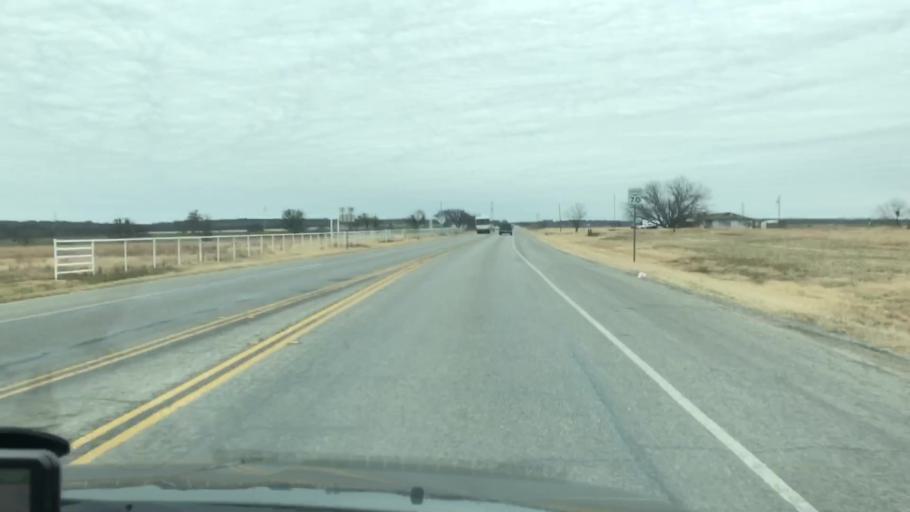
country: US
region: Texas
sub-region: Palo Pinto County
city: Mineral Wells
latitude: 32.9214
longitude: -98.0745
